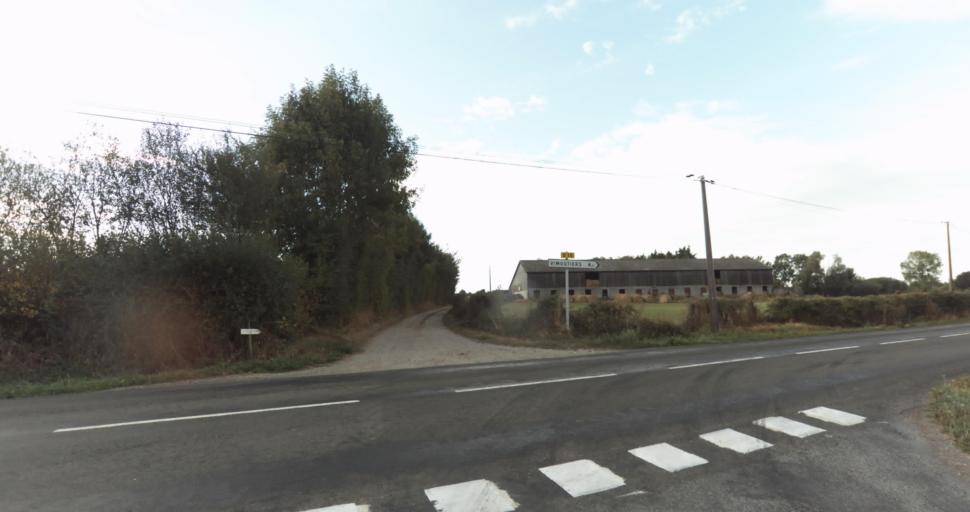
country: FR
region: Lower Normandy
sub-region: Departement de l'Orne
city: Vimoutiers
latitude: 48.9444
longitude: 0.2421
